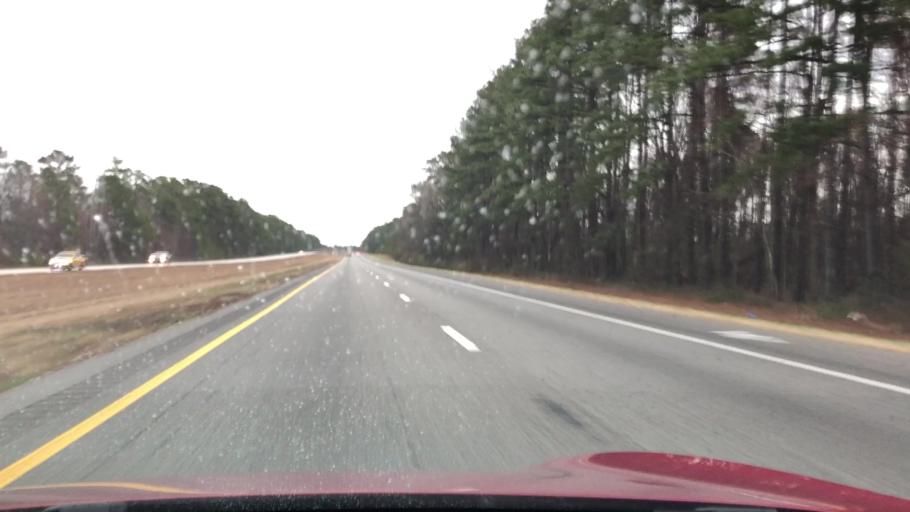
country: US
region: South Carolina
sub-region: Dillon County
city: Latta
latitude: 34.3889
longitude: -79.4636
